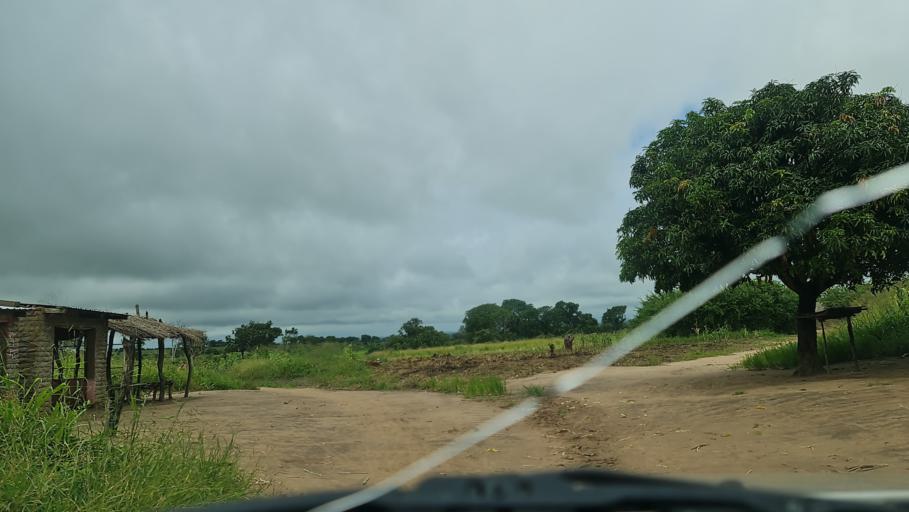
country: MW
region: Southern Region
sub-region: Nsanje District
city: Nsanje
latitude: -17.3381
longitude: 35.7190
